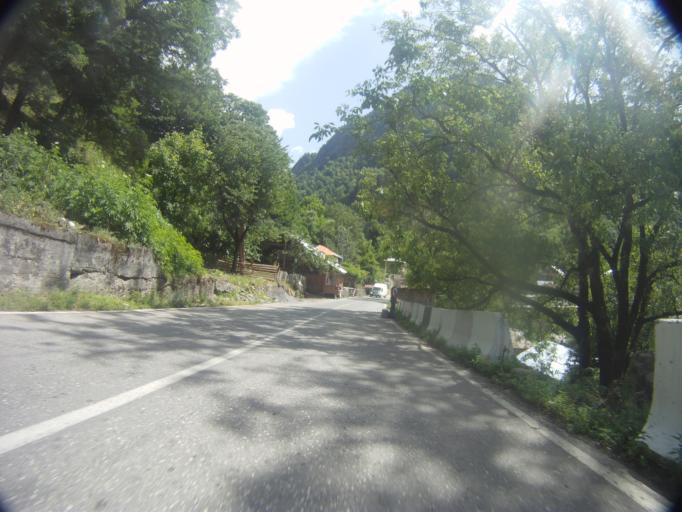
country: GE
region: Samegrelo and Zemo Svaneti
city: Jvari
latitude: 42.9457
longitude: 42.1888
